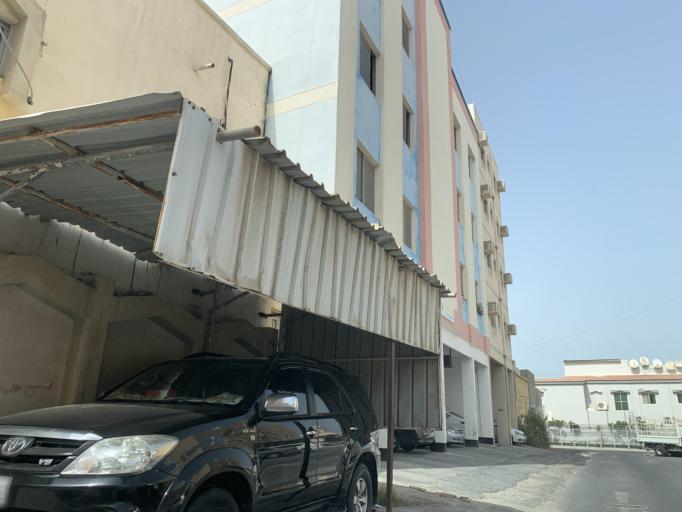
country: BH
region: Northern
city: Ar Rifa'
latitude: 26.1227
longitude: 50.5737
